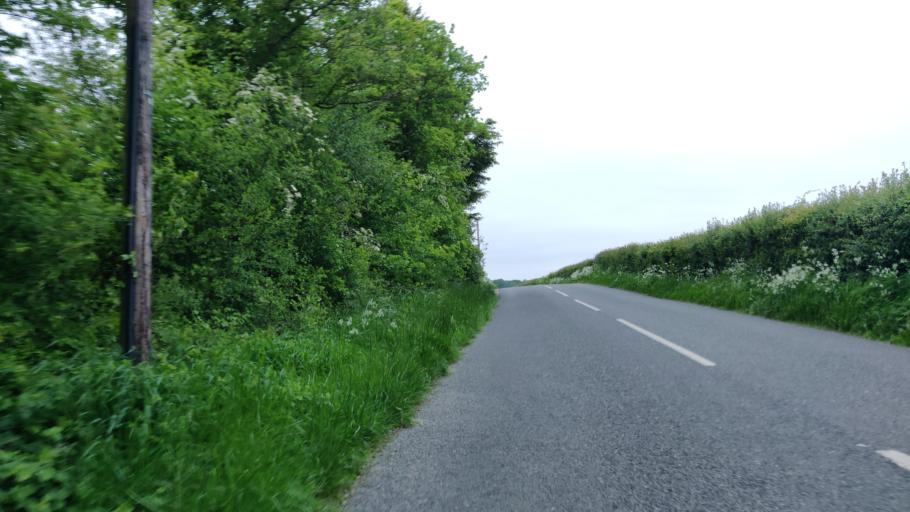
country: GB
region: England
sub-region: West Sussex
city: Partridge Green
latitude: 50.9722
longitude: -0.3023
